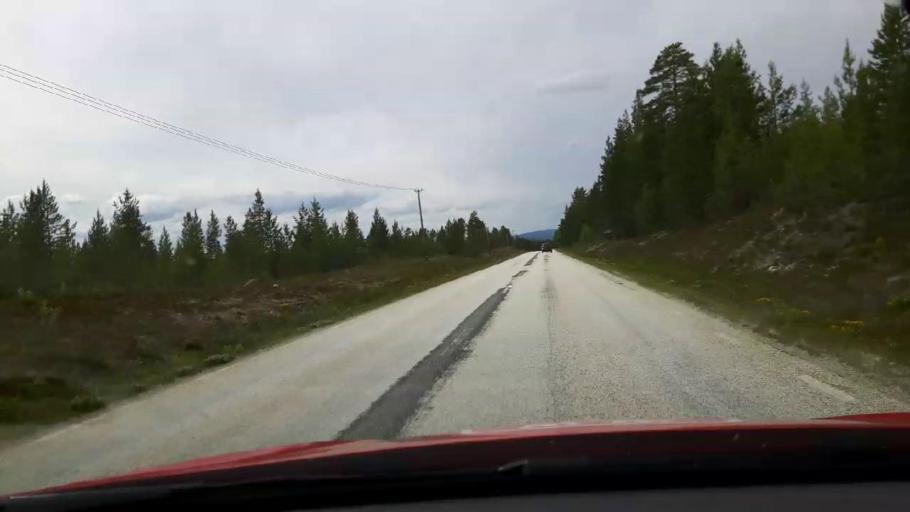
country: SE
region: Jaemtland
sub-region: Harjedalens Kommun
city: Sveg
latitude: 62.4059
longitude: 13.7221
